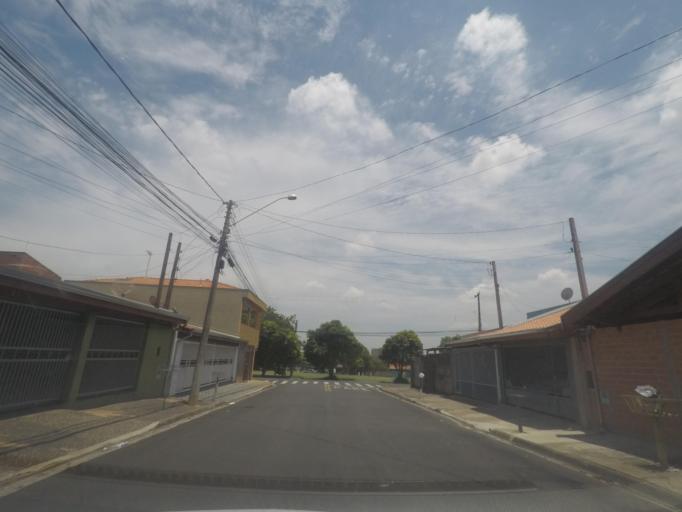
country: BR
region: Sao Paulo
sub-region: Nova Odessa
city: Nova Odessa
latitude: -22.7965
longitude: -47.2800
